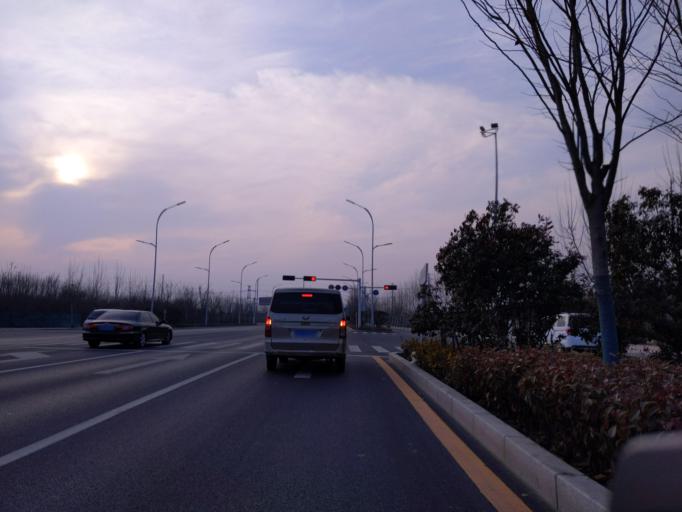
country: CN
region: Henan Sheng
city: Puyang
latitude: 35.8184
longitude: 115.0042
